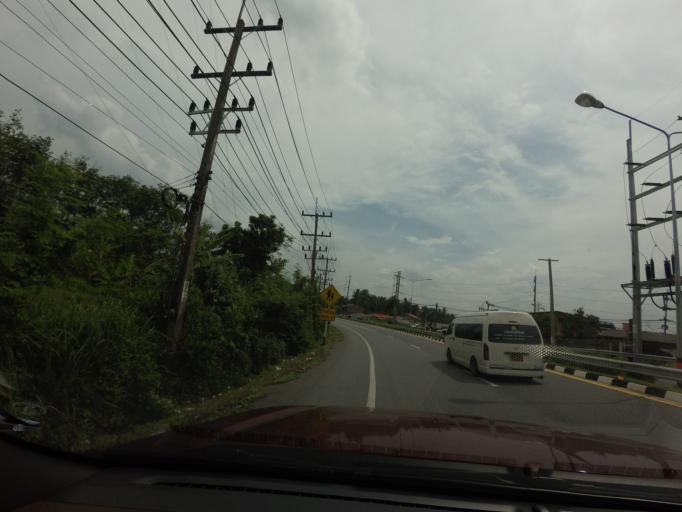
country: TH
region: Yala
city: Yala
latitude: 6.5008
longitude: 101.2686
